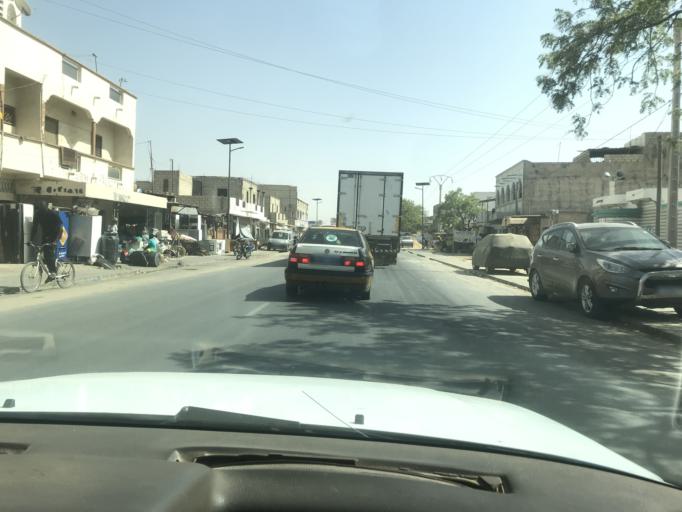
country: SN
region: Saint-Louis
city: Saint-Louis
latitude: 15.9993
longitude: -16.4877
